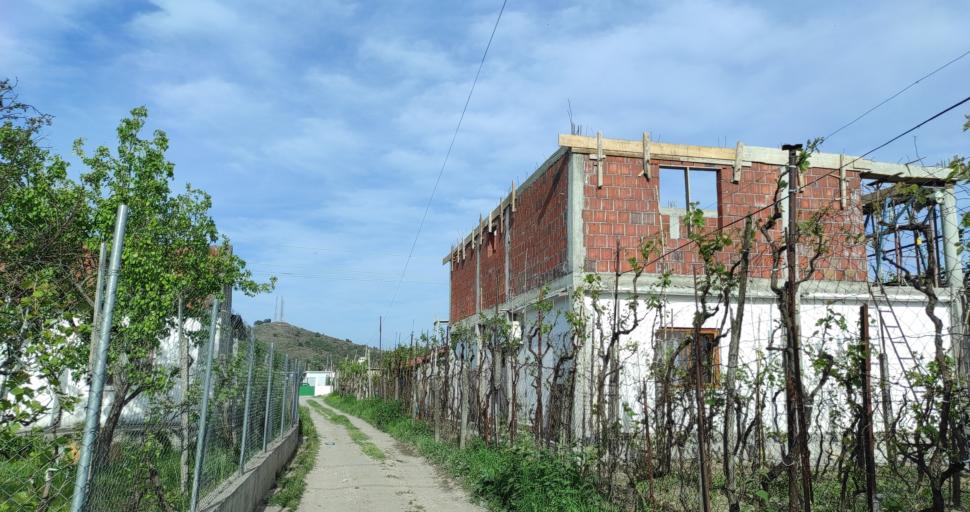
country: AL
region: Shkoder
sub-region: Rrethi i Shkodres
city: Shkoder
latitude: 42.0615
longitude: 19.5281
